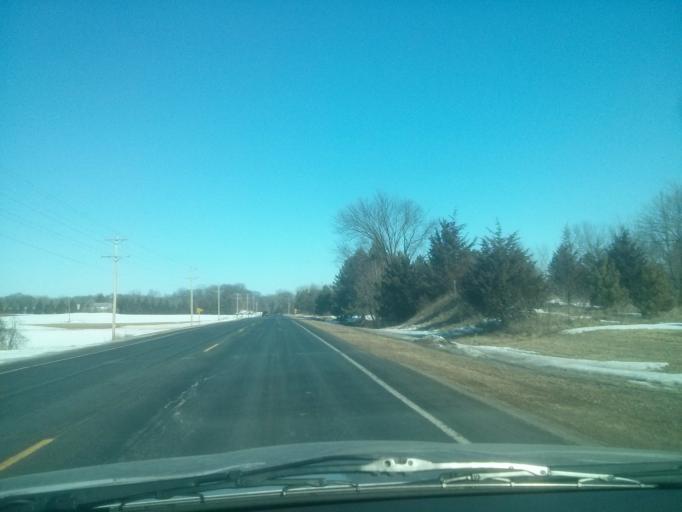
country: US
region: Minnesota
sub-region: Washington County
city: Bayport
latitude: 45.0624
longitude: -92.7408
